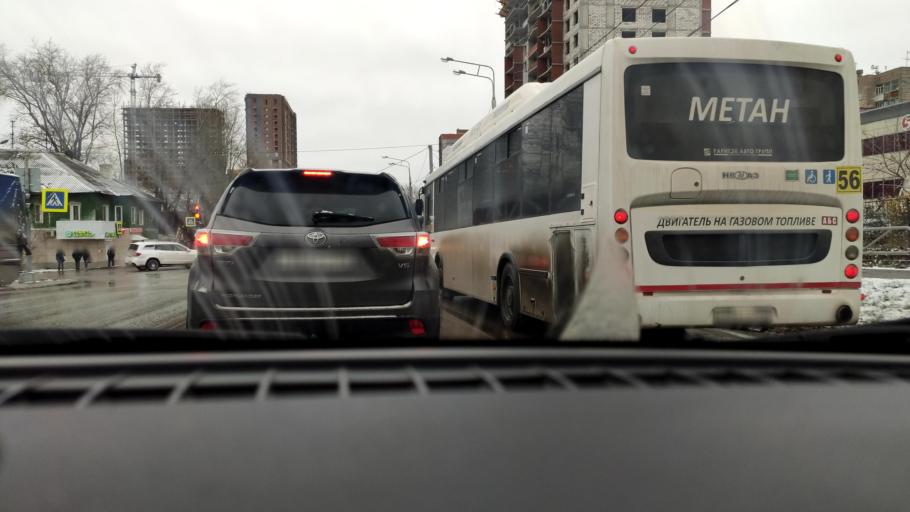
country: RU
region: Perm
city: Perm
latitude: 57.9799
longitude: 56.2159
